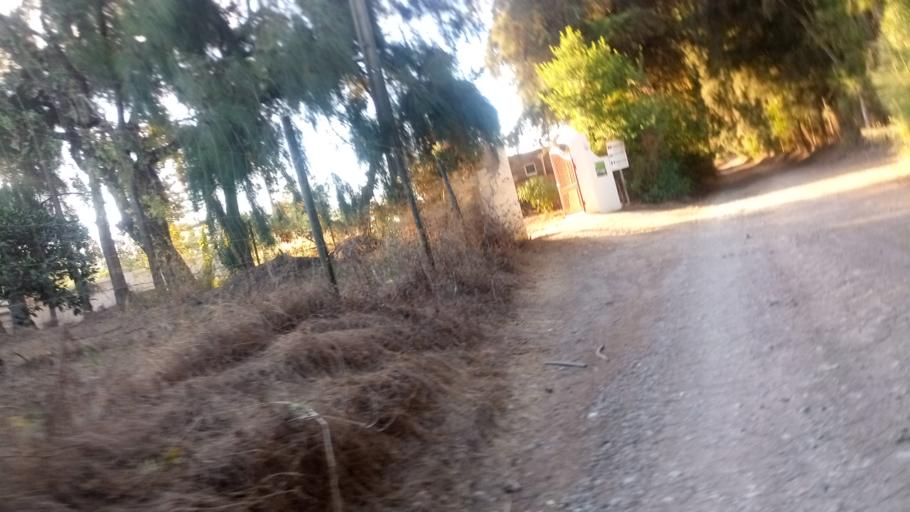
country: PT
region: Faro
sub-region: Tavira
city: Tavira
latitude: 37.1529
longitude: -7.5744
